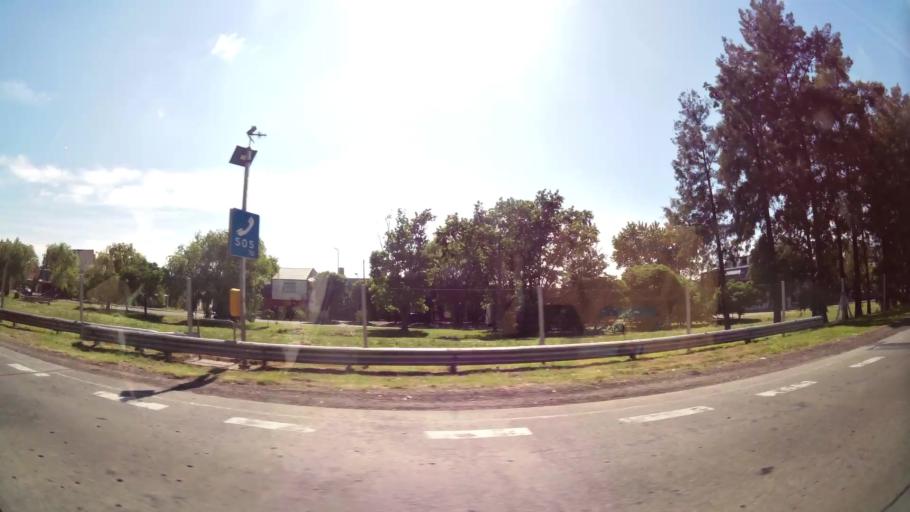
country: AR
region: Buenos Aires
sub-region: Partido de Tigre
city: Tigre
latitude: -34.4582
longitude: -58.5730
